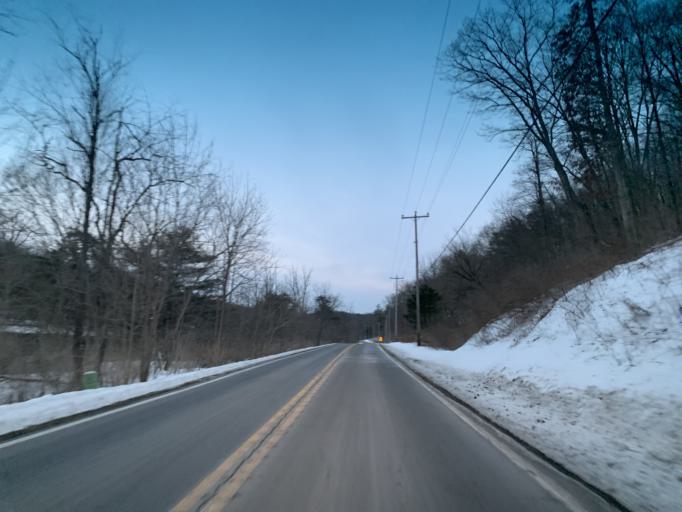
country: US
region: Maryland
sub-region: Allegany County
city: Cumberland
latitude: 39.6815
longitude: -78.4923
